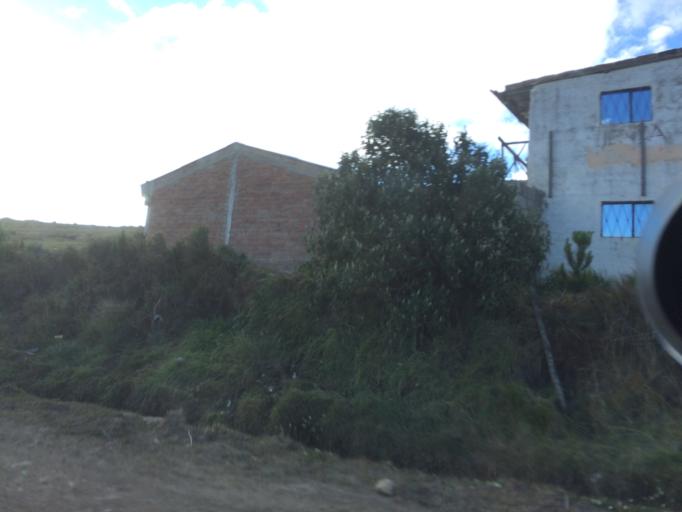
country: EC
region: Chimborazo
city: Alausi
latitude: -2.2476
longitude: -78.6604
